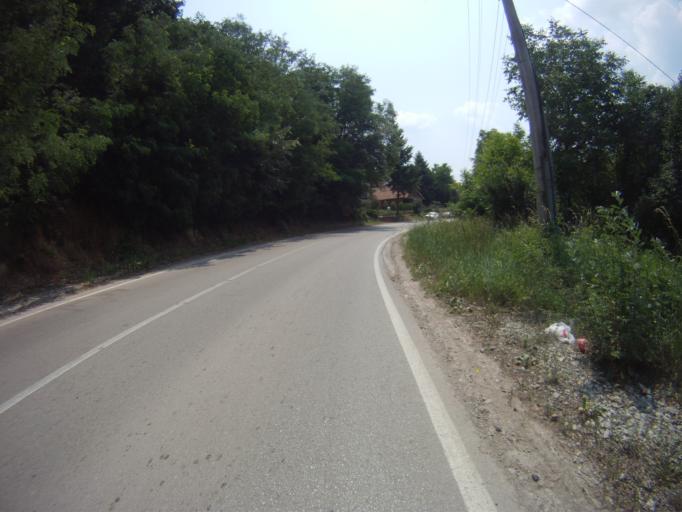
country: RS
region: Central Serbia
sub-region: Nisavski Okrug
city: Gadzin Han
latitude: 43.2294
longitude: 22.0322
